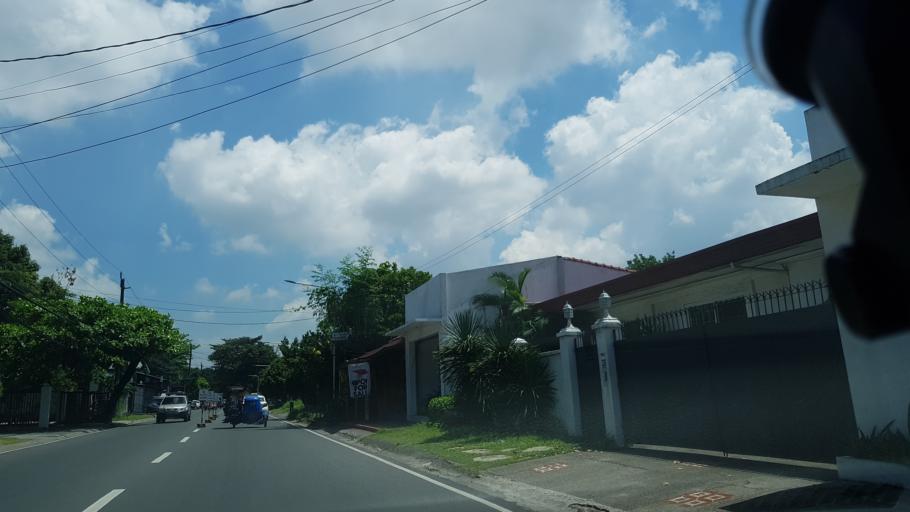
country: PH
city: Sambayanihan People's Village
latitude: 14.4490
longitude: 121.0076
